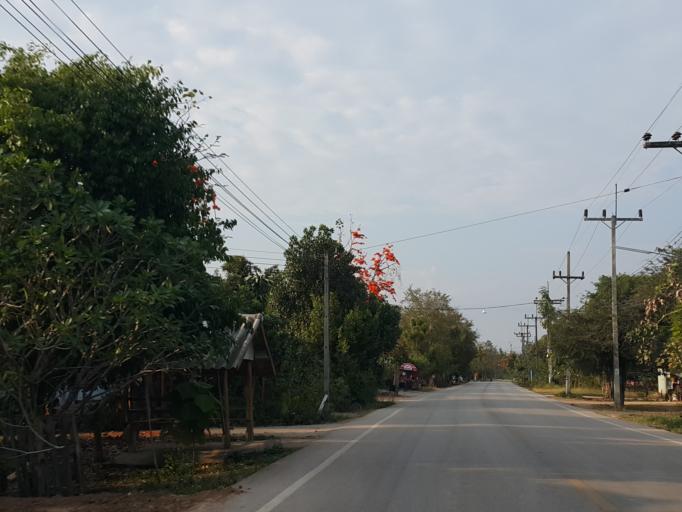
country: TH
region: Lampang
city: Chae Hom
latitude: 18.5496
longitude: 99.4768
